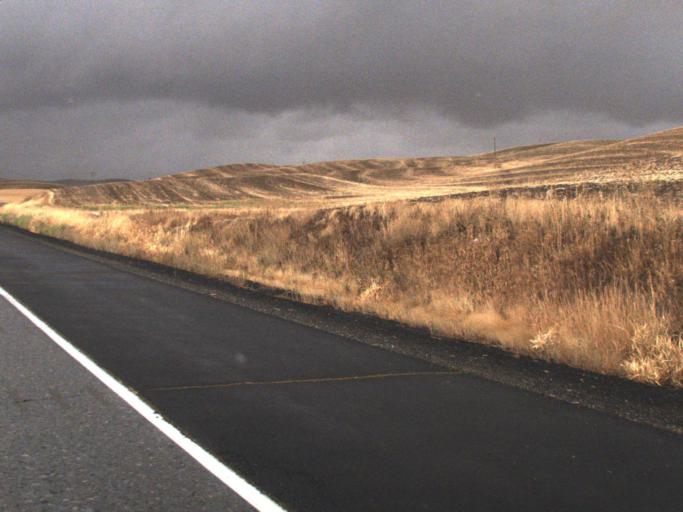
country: US
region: Washington
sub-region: Whitman County
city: Colfax
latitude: 47.0456
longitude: -117.3780
